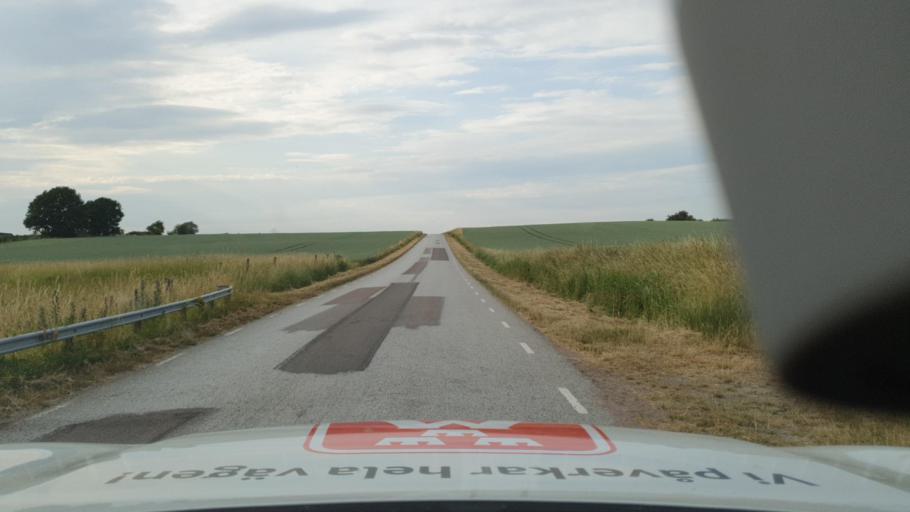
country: SE
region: Skane
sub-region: Sjobo Kommun
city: Sjoebo
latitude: 55.6461
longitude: 13.8153
